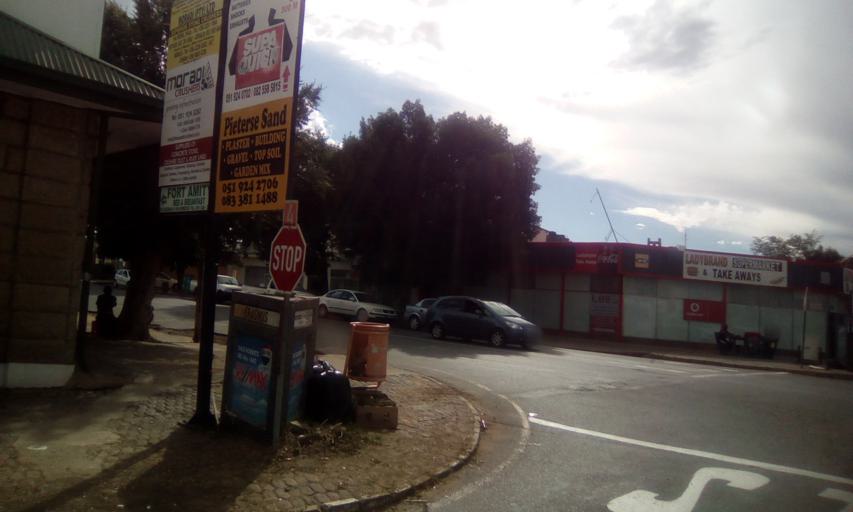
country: ZA
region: Orange Free State
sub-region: Thabo Mofutsanyana District Municipality
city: Ladybrand
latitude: -29.1966
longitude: 27.4588
